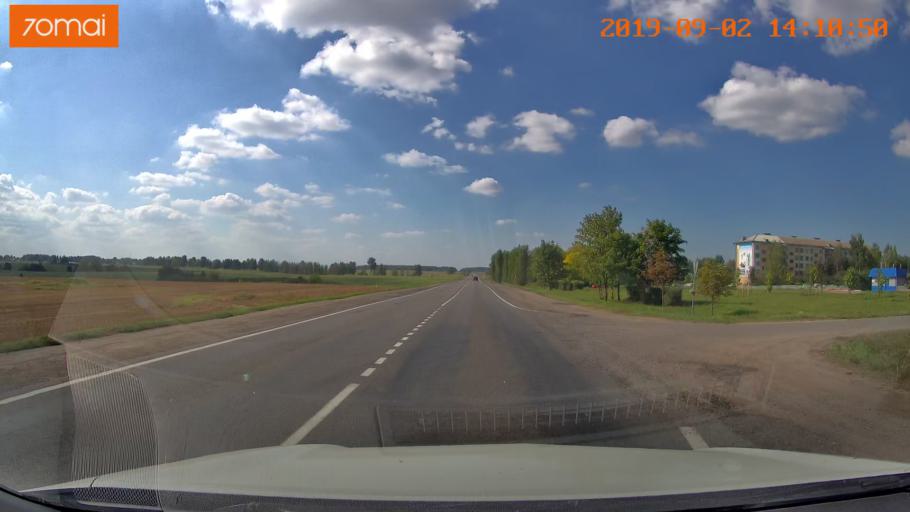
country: BY
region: Mogilev
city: Chavusy
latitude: 53.8011
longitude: 30.9615
